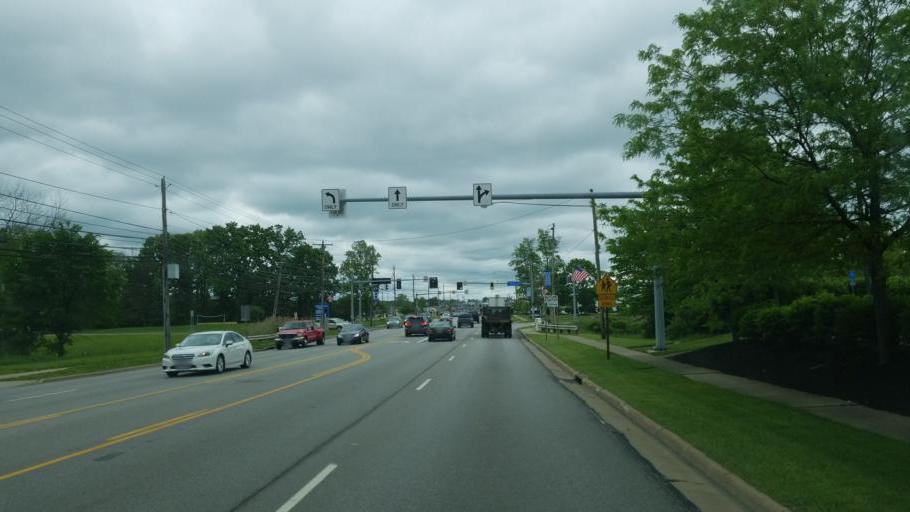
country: US
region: Ohio
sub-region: Medina County
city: Brunswick
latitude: 41.2382
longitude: -81.8182
